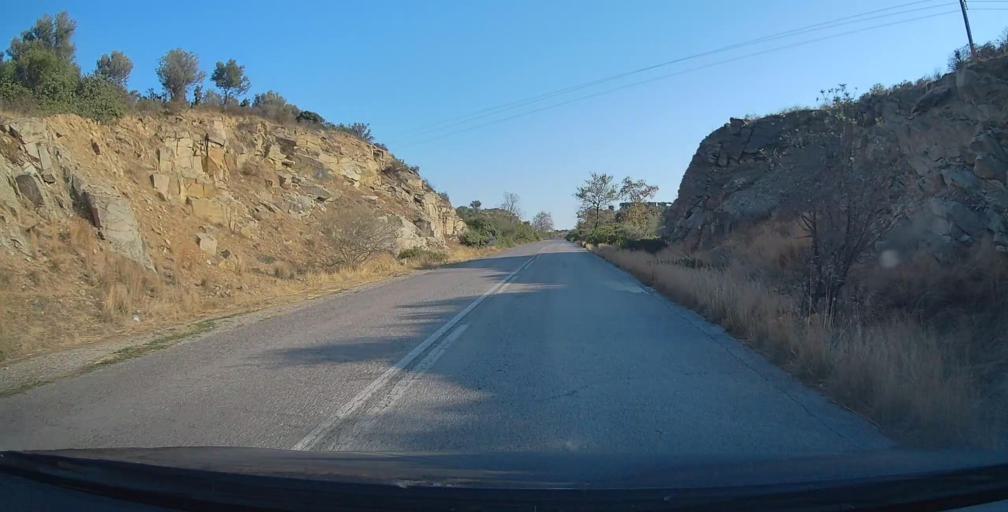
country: GR
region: Central Macedonia
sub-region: Nomos Chalkidikis
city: Sykia
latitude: 40.0134
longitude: 23.8746
